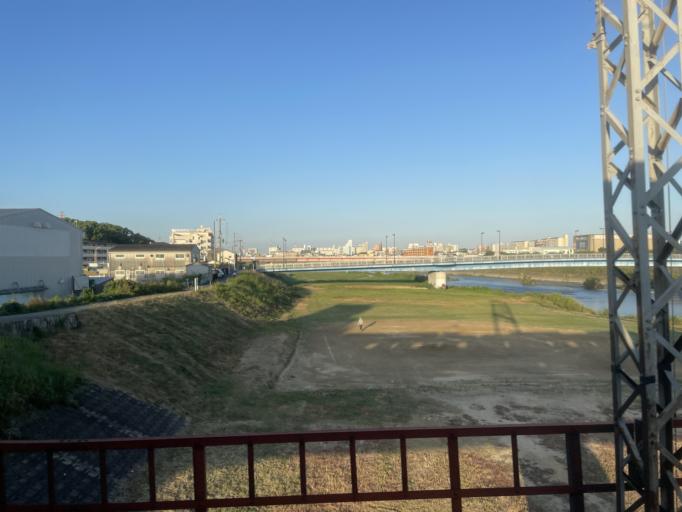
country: JP
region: Osaka
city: Matsubara
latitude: 34.5969
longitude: 135.5325
